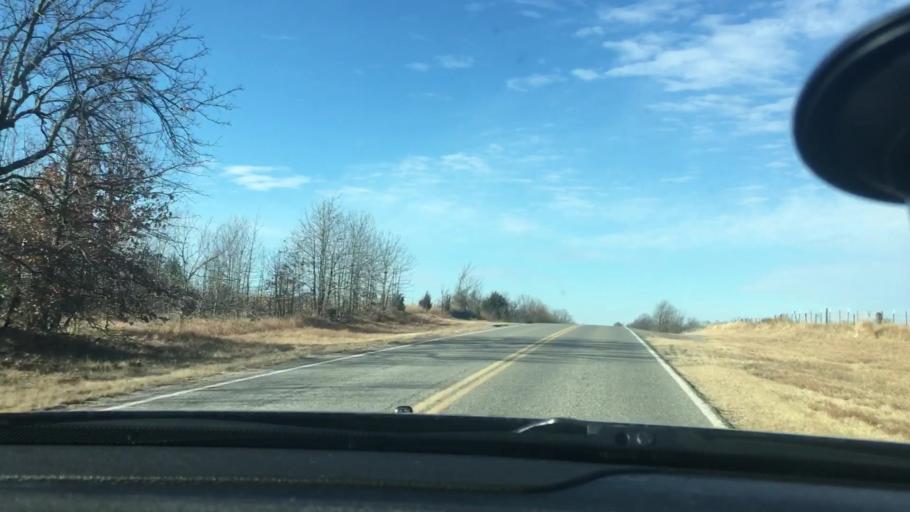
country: US
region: Oklahoma
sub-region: Seminole County
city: Konawa
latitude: 34.9856
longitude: -96.8404
